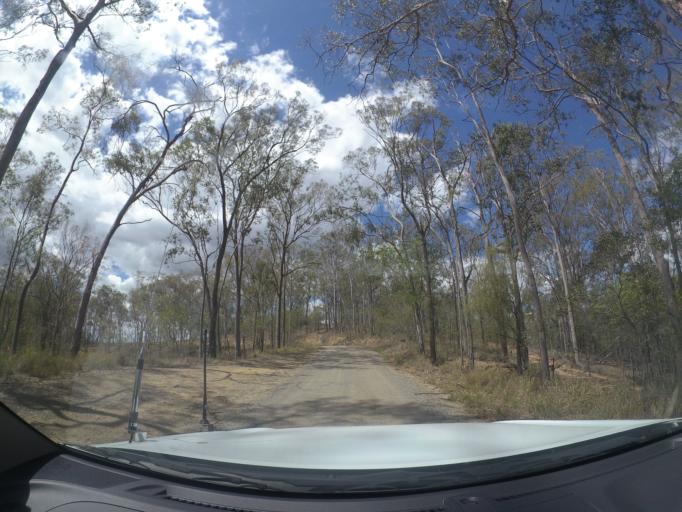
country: AU
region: Queensland
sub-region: Logan
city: Cedar Vale
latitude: -27.8953
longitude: 153.0453
